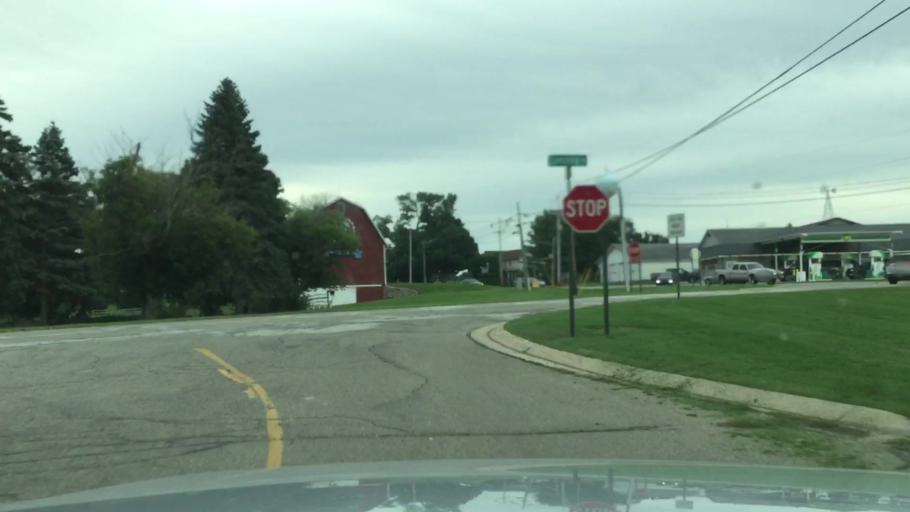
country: US
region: Michigan
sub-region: Shiawassee County
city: Durand
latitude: 42.8840
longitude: -84.0688
